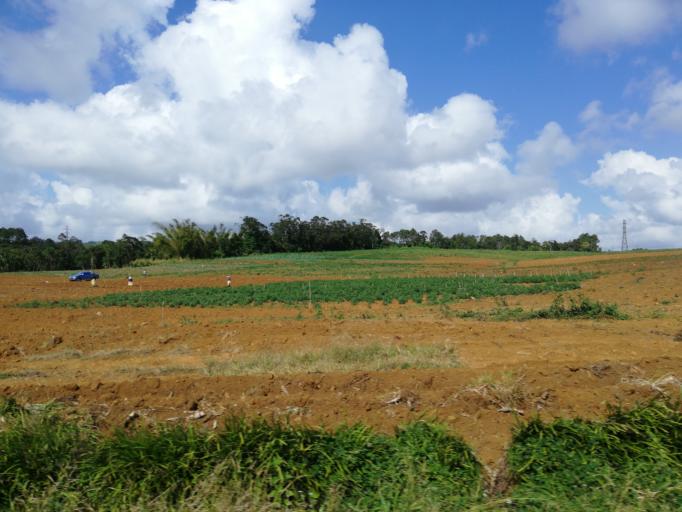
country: MU
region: Pamplemousses
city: Creve Coeur
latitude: -20.2072
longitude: 57.5582
